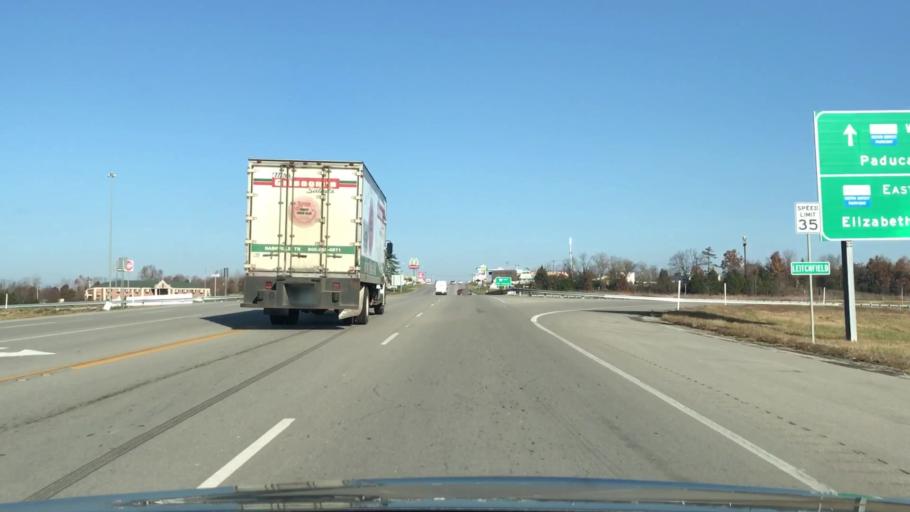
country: US
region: Kentucky
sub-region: Grayson County
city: Leitchfield
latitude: 37.4649
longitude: -86.2919
